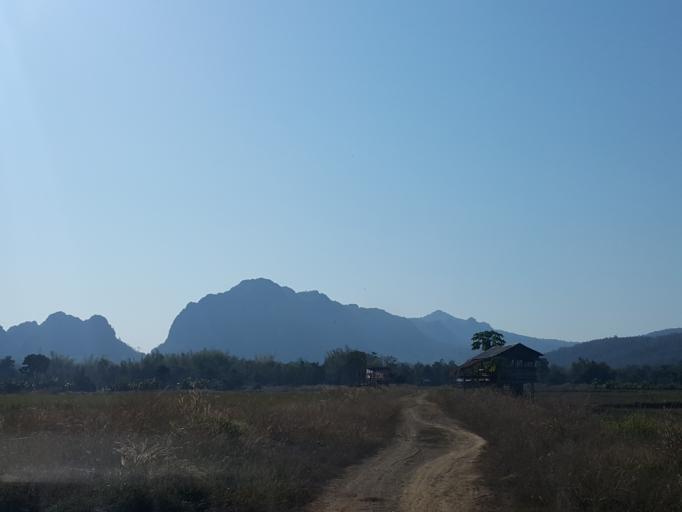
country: TH
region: Sukhothai
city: Thung Saliam
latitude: 17.3167
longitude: 99.4347
